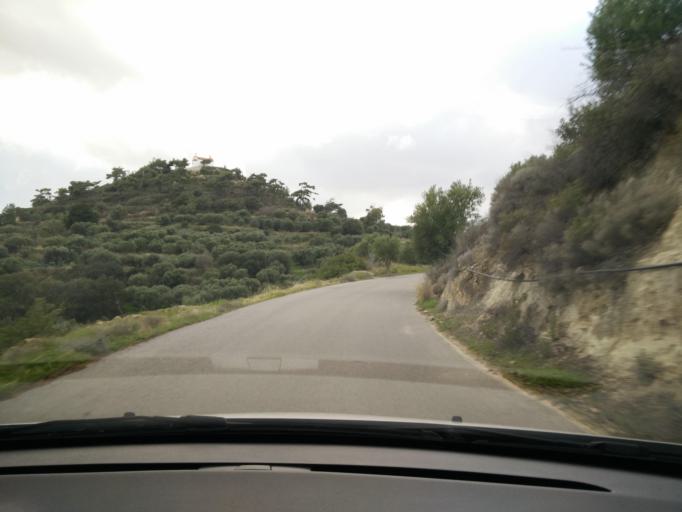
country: GR
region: Crete
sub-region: Nomos Lasithiou
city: Kritsa
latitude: 35.0967
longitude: 25.6902
